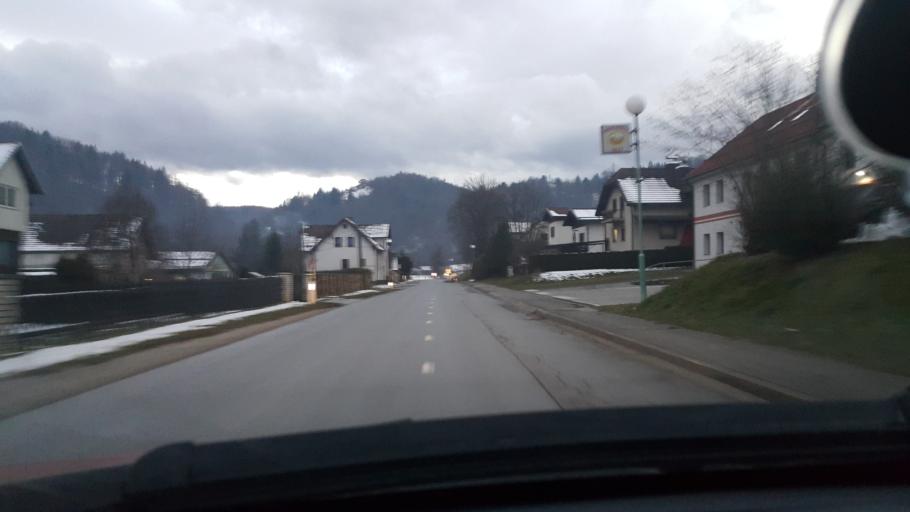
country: SI
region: Kungota
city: Zgornja Kungota
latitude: 46.6379
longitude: 15.6136
